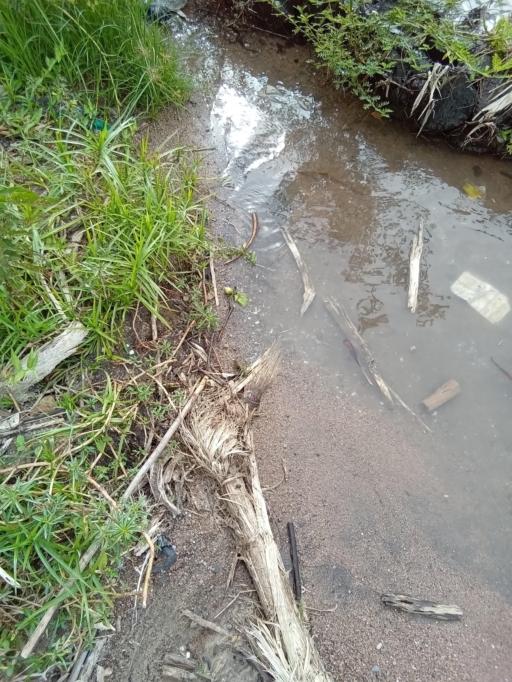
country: KE
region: Homa Bay
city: Homa Bay
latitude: -0.4700
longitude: 34.1767
